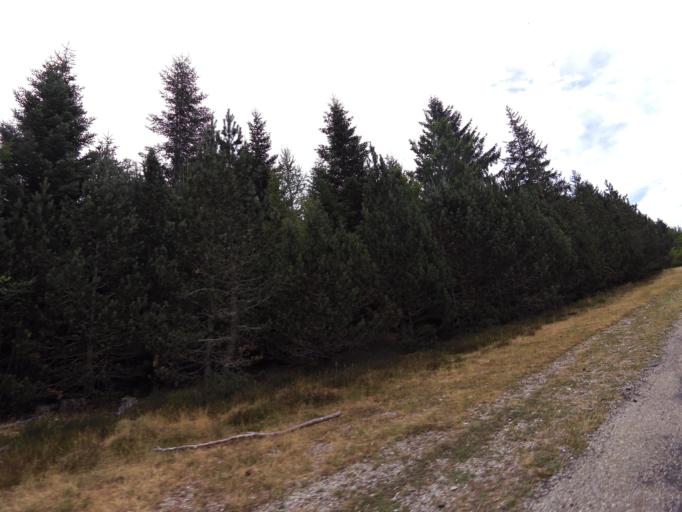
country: FR
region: Languedoc-Roussillon
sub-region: Departement du Gard
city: Valleraugue
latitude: 44.0775
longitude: 3.5778
